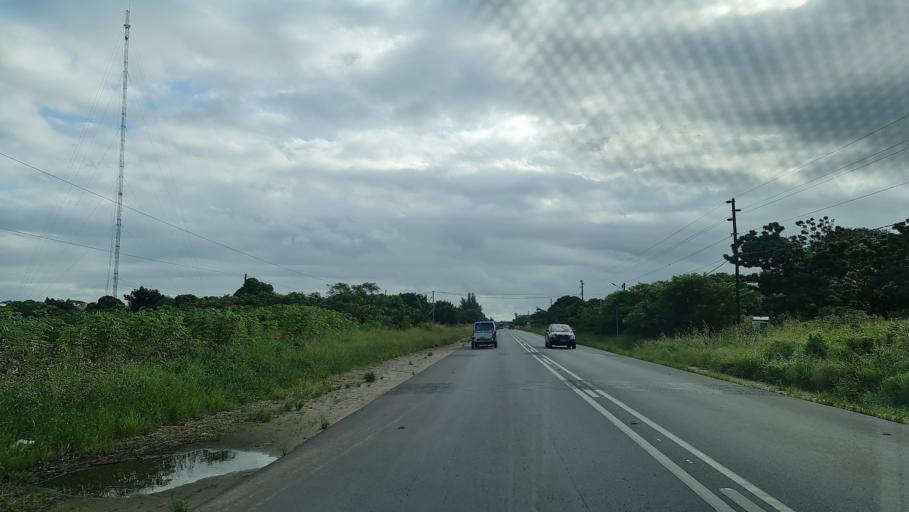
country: MZ
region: Maputo
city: Manhica
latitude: -25.4180
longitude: 32.7325
